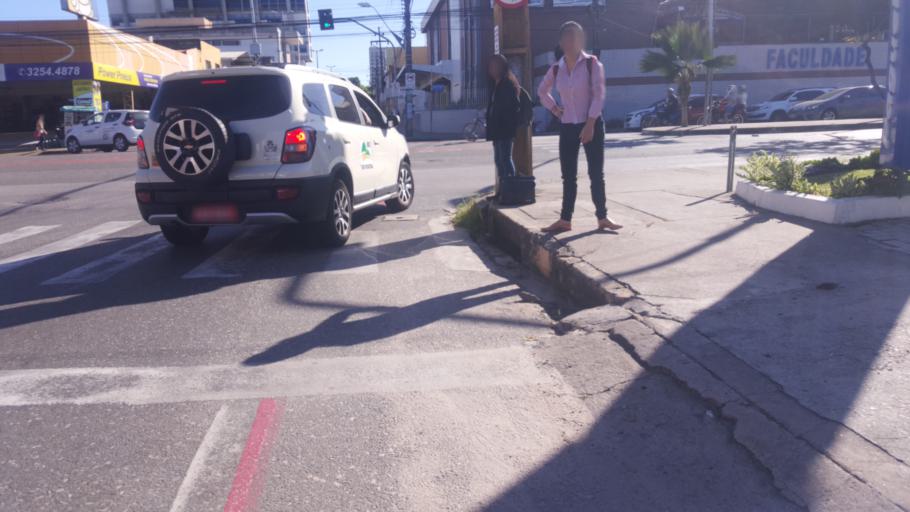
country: BR
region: Ceara
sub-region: Fortaleza
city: Fortaleza
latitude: -3.7368
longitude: -38.5316
